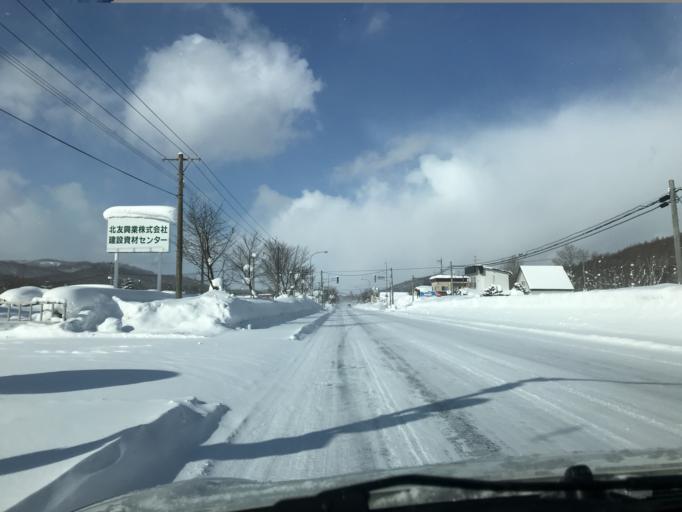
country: JP
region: Hokkaido
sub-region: Asahikawa-shi
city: Asahikawa
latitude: 43.9232
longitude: 142.4769
